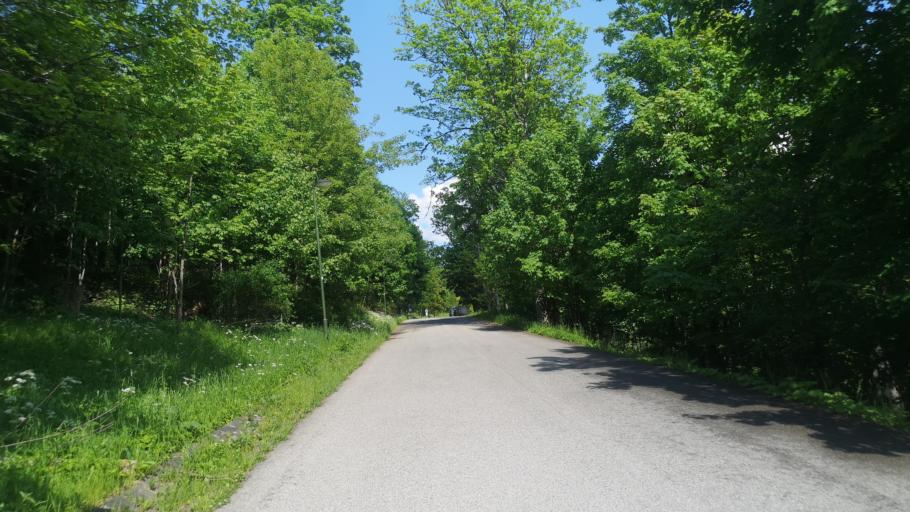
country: SK
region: Presovsky
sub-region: Okres Poprad
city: Vysoke Tatry
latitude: 49.1697
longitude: 20.2769
